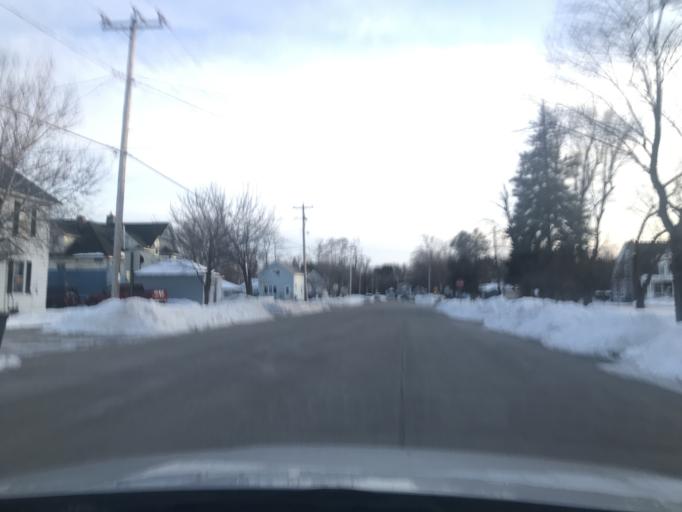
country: US
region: Wisconsin
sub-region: Marinette County
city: Peshtigo
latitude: 45.0535
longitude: -87.7419
